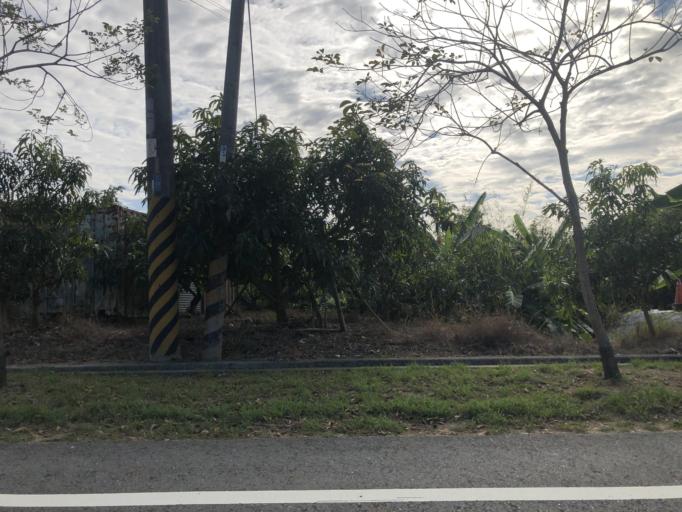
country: TW
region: Taiwan
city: Yujing
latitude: 23.0522
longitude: 120.4175
